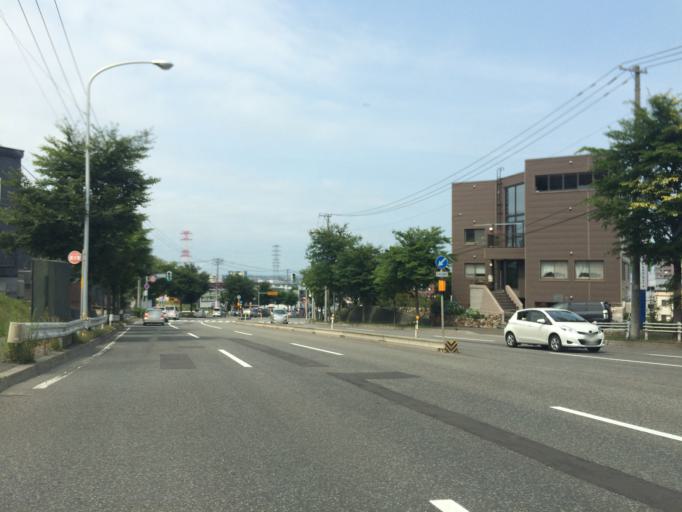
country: JP
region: Hokkaido
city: Sapporo
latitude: 43.0925
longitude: 141.2602
